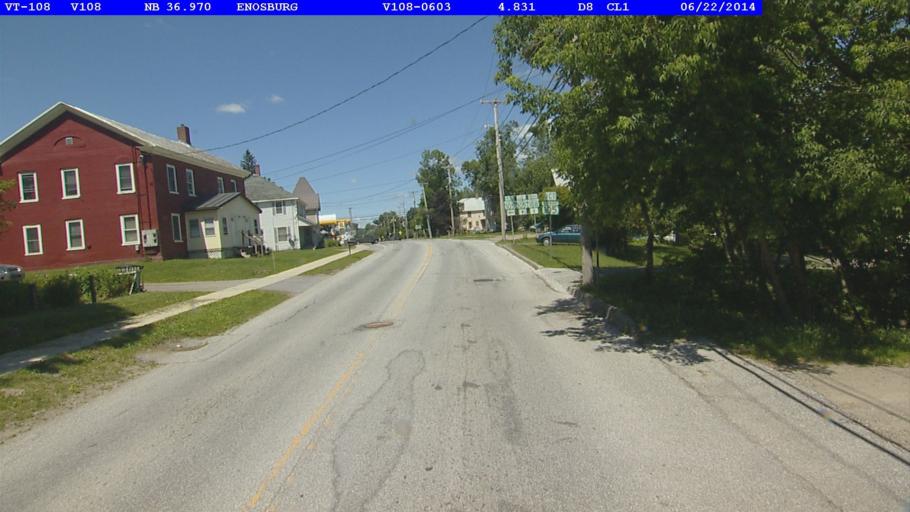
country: US
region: Vermont
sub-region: Franklin County
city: Enosburg Falls
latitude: 44.9034
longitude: -72.8072
